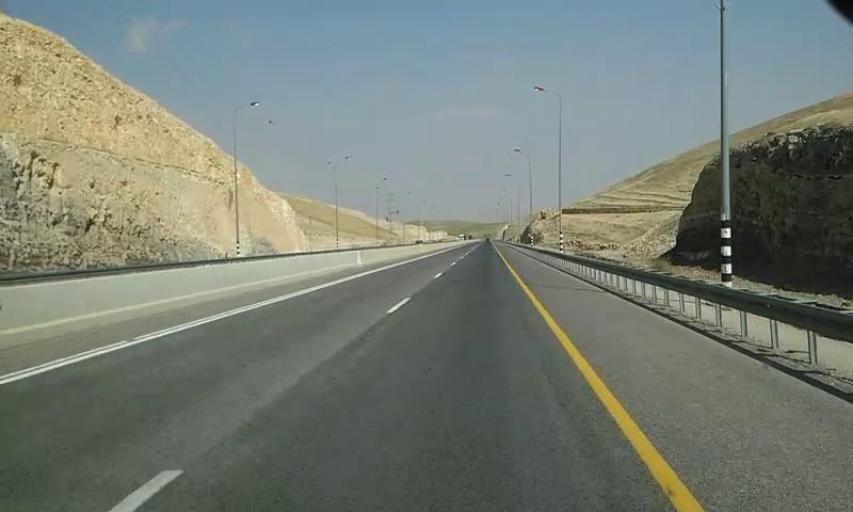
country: PS
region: West Bank
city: Jericho
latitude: 31.8176
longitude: 35.3750
